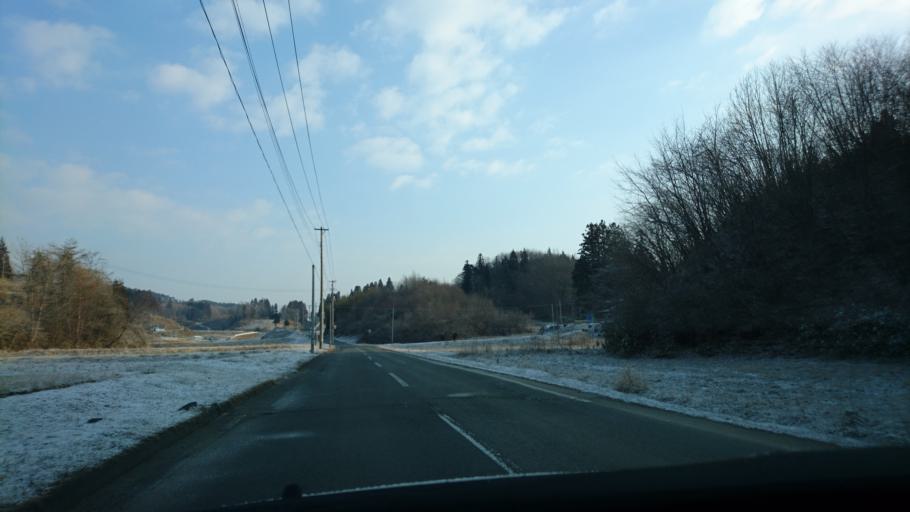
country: JP
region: Iwate
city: Ichinoseki
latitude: 38.9072
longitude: 141.3764
